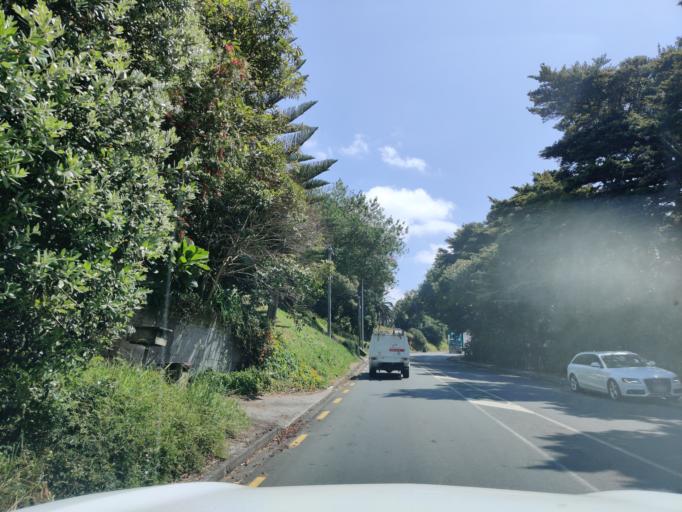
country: NZ
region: Auckland
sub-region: Auckland
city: Pukekohe East
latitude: -37.1980
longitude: 174.9128
